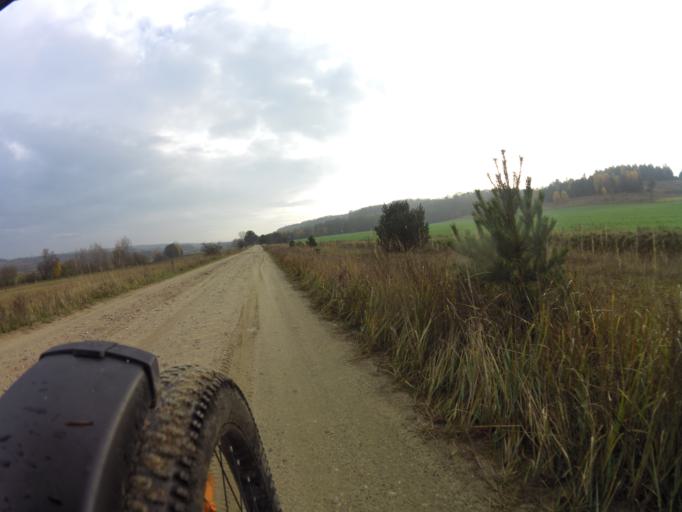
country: PL
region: Pomeranian Voivodeship
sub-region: Powiat wejherowski
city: Gniewino
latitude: 54.7075
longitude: 18.1012
